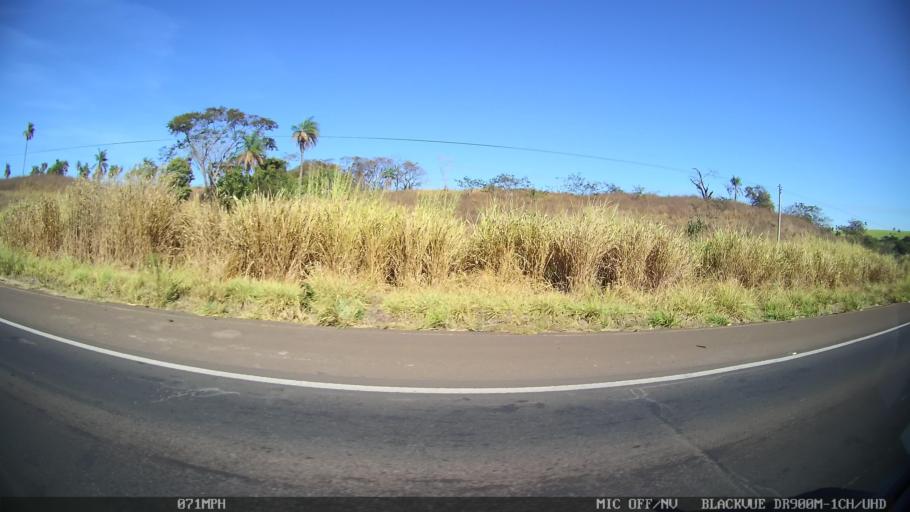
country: BR
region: Sao Paulo
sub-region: Olimpia
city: Olimpia
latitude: -20.6320
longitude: -48.8129
